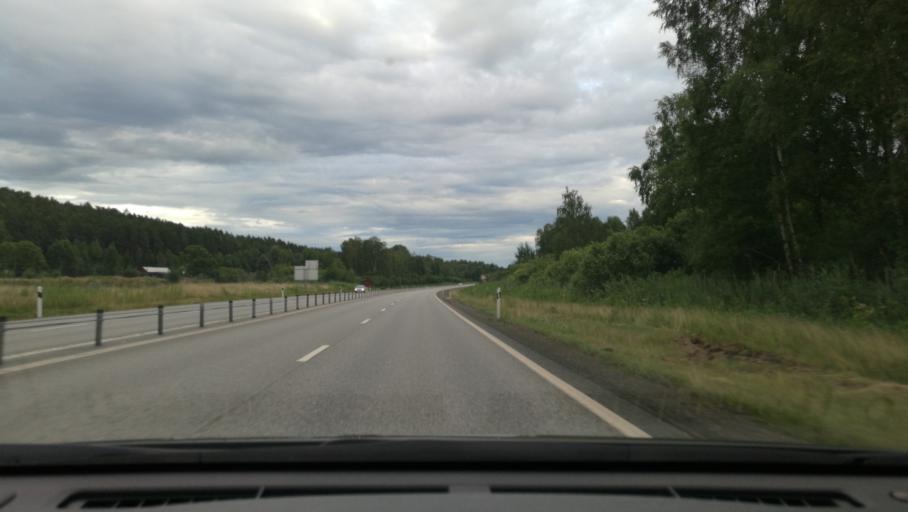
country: SE
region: OEstergoetland
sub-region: Norrkopings Kommun
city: Svartinge
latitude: 58.6457
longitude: 16.0690
